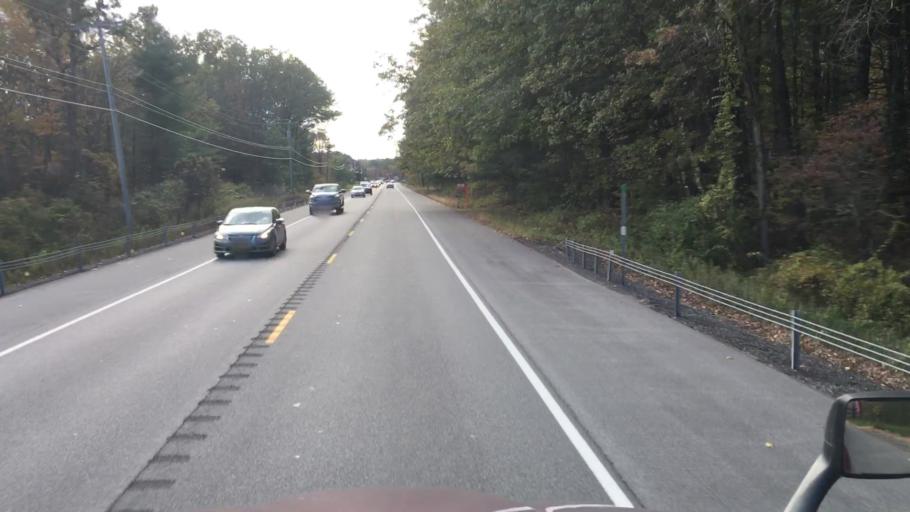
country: US
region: New York
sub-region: Saratoga County
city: North Ballston Spa
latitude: 43.0270
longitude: -73.8341
